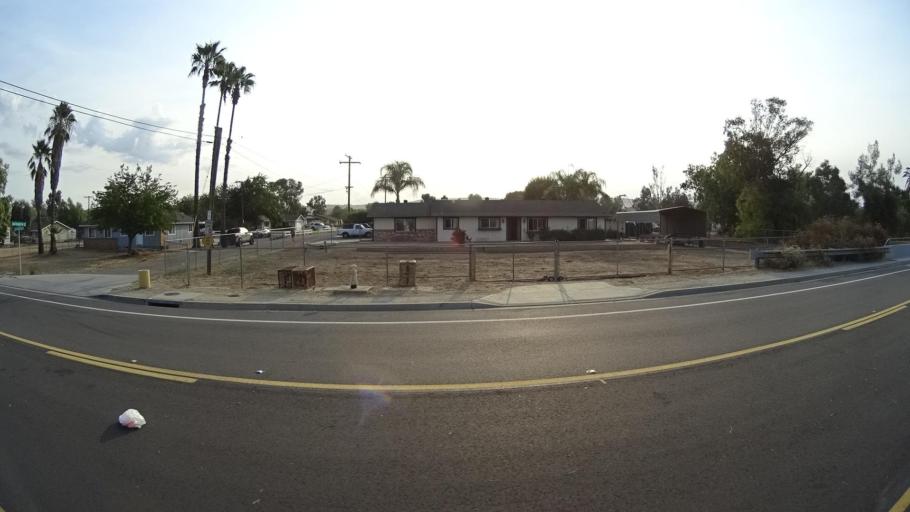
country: US
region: California
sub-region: San Diego County
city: Ramona
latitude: 33.0279
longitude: -116.8664
